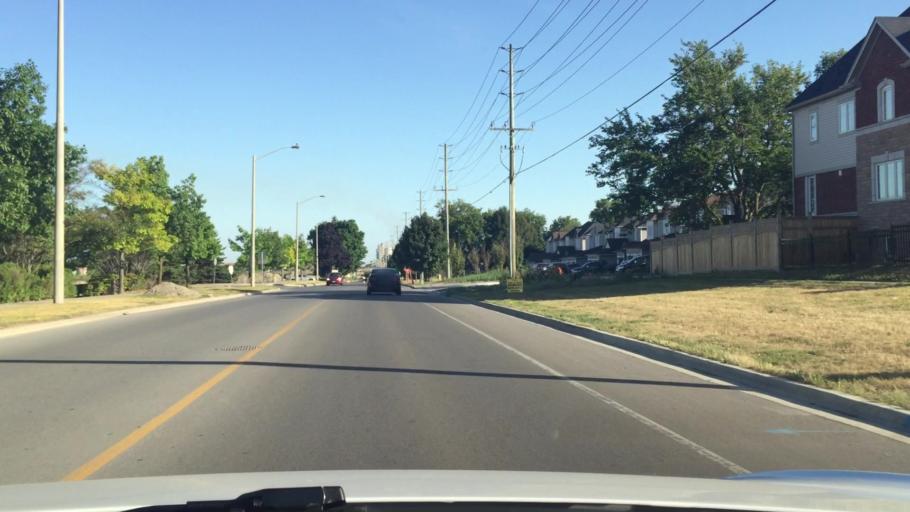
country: CA
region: Ontario
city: Oshawa
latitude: 43.9082
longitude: -78.7116
